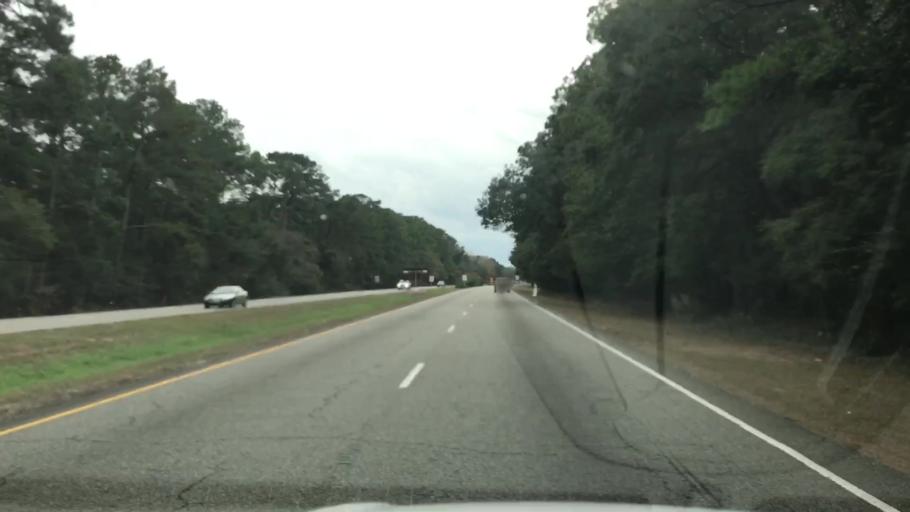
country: US
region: South Carolina
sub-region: Georgetown County
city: Murrells Inlet
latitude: 33.5007
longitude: -79.0829
